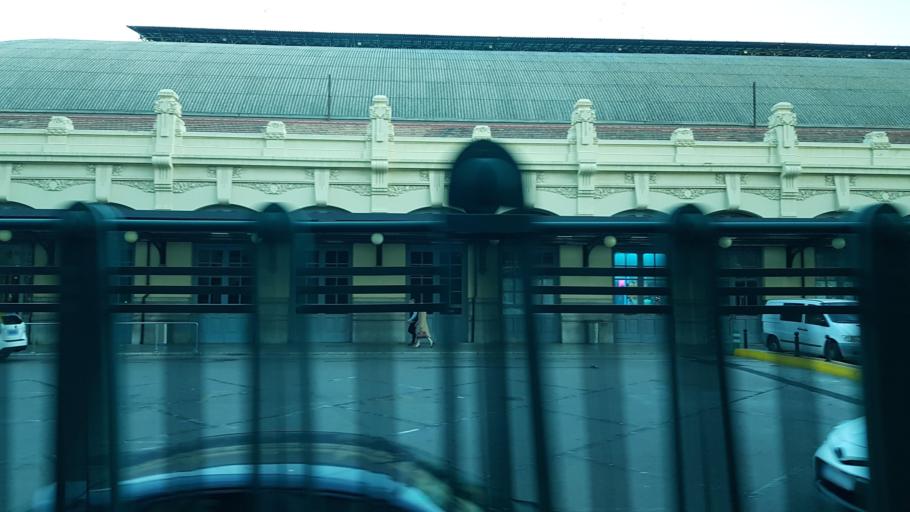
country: ES
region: Valencia
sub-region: Provincia de Valencia
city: Valencia
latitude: 39.4667
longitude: -0.3781
